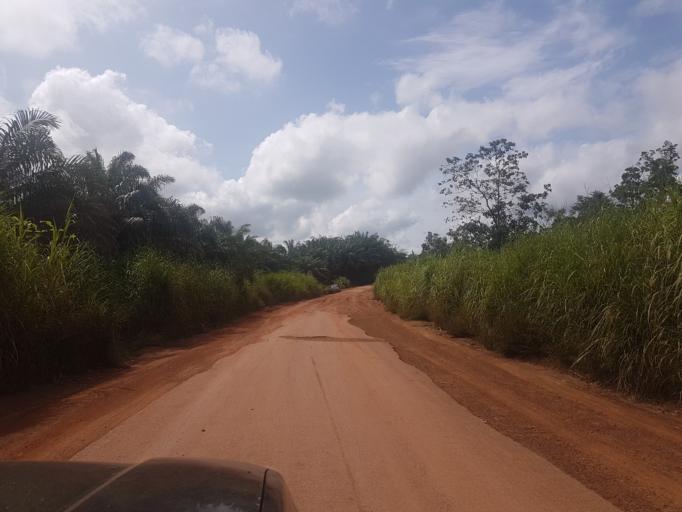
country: GN
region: Nzerekore
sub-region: Prefecture de Guekedou
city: Gueckedou
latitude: 8.6751
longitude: -10.1204
